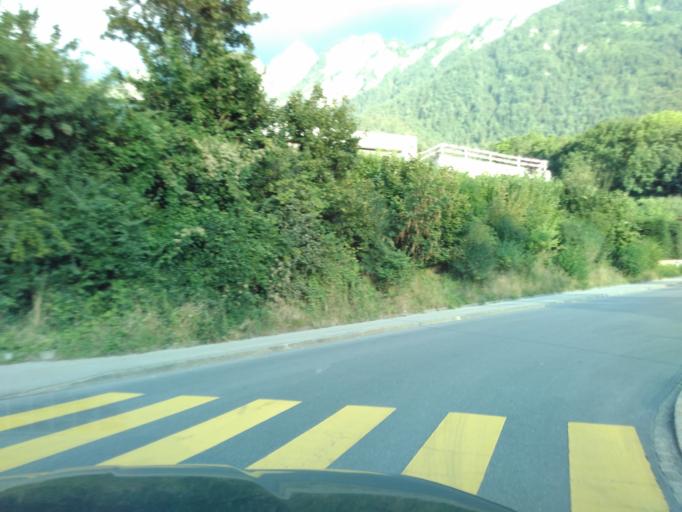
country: CH
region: Grisons
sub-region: Plessur District
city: Chur
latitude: 46.8622
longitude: 9.5421
